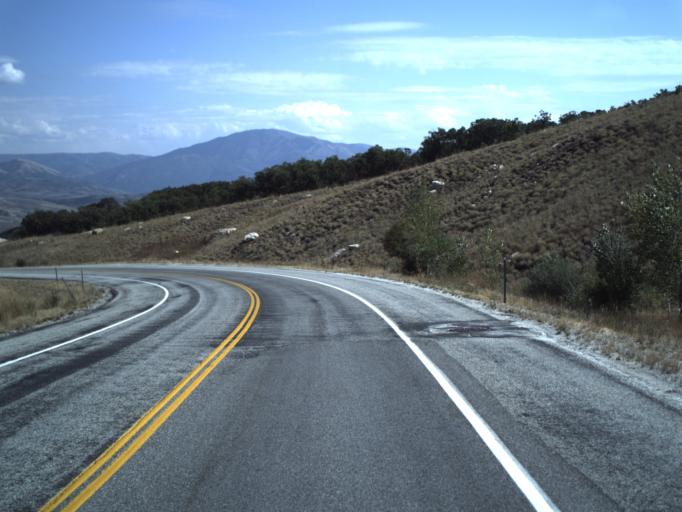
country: US
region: Utah
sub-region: Morgan County
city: Mountain Green
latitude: 41.2090
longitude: -111.8402
